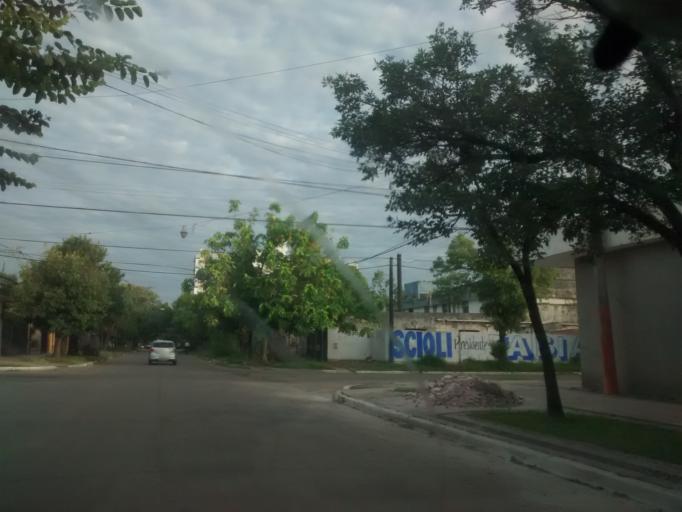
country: AR
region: Chaco
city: Resistencia
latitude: -27.4624
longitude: -58.9774
